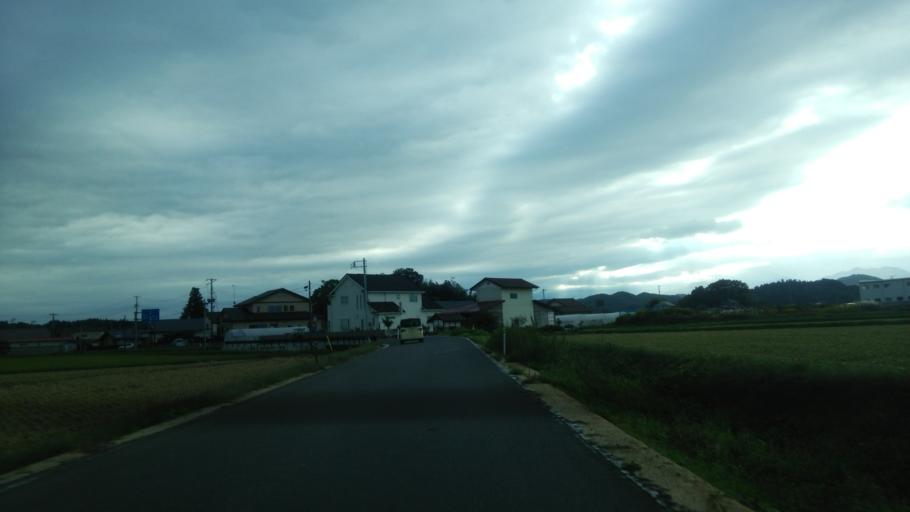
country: JP
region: Fukushima
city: Sukagawa
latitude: 37.2753
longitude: 140.2823
